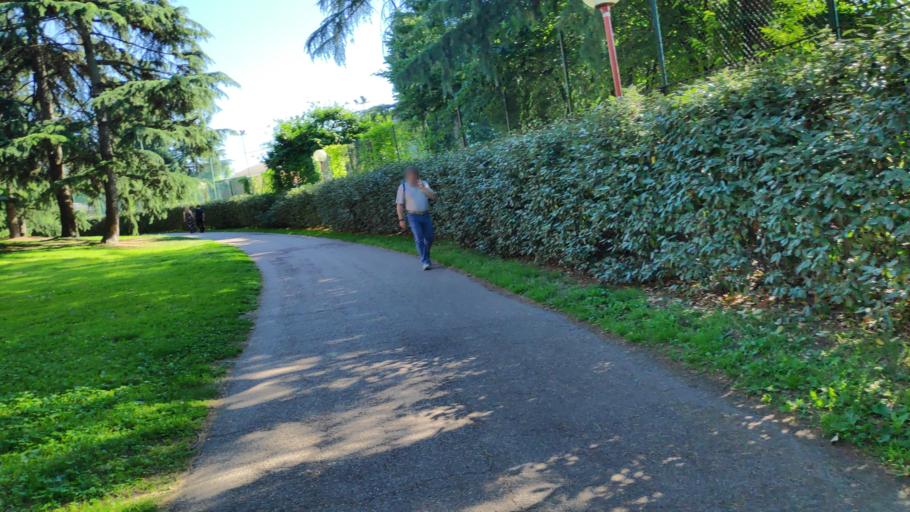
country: IT
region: Lombardy
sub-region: Citta metropolitana di Milano
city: Basiglio
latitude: 45.3576
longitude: 9.1589
